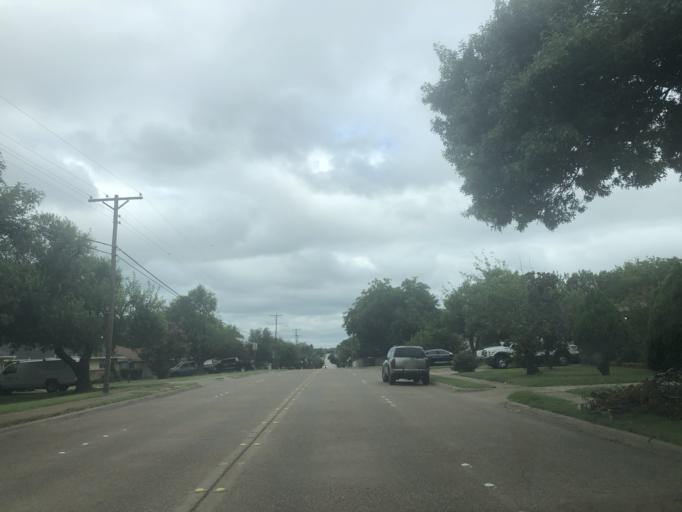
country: US
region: Texas
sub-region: Dallas County
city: Duncanville
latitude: 32.6518
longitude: -96.9146
